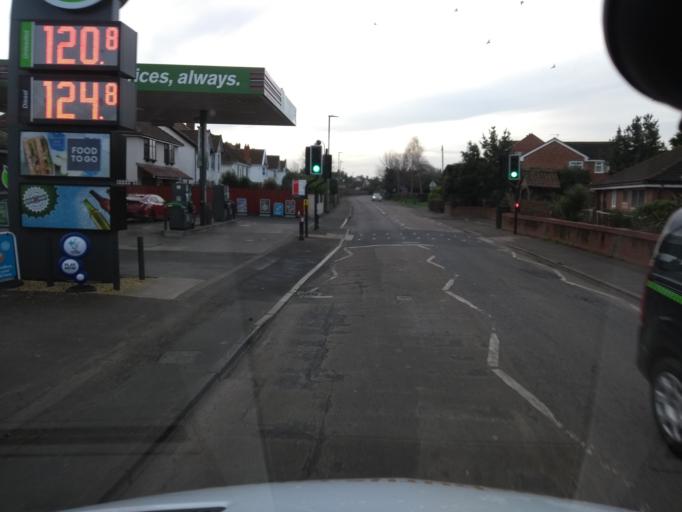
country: GB
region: England
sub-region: Somerset
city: Burnham-on-Sea
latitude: 51.2517
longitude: -2.9983
